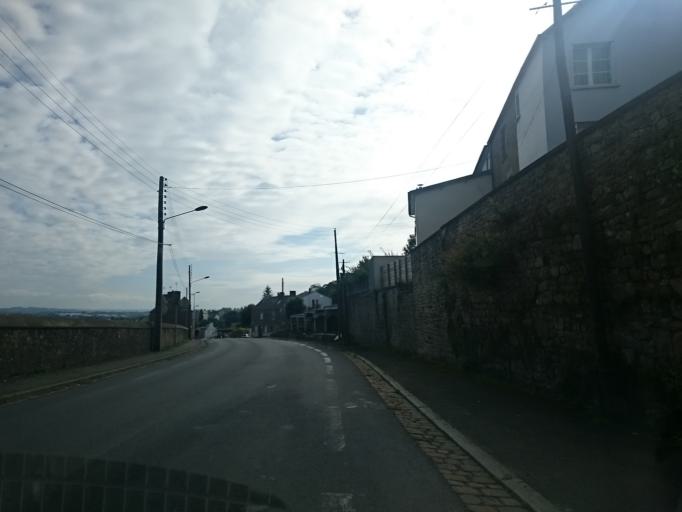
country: FR
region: Lower Normandy
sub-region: Departement de la Manche
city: Avranches
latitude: 48.6898
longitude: -1.3576
